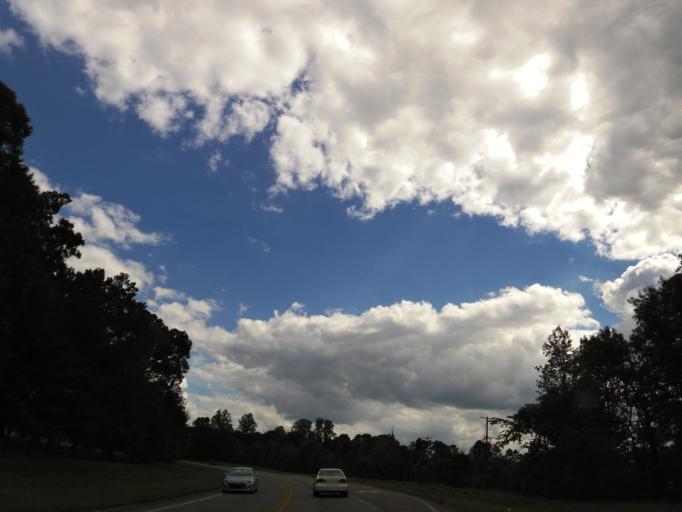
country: US
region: Georgia
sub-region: Walker County
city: Lookout Mountain
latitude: 34.9655
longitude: -85.3386
